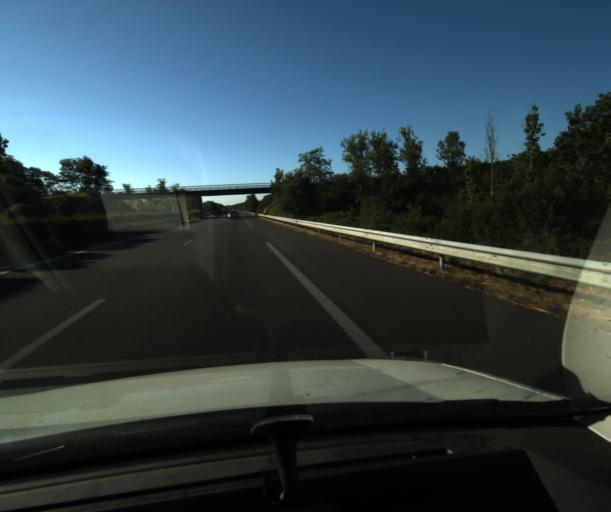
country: FR
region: Midi-Pyrenees
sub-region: Departement du Tarn-et-Garonne
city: Montech
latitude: 44.0001
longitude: 1.2259
